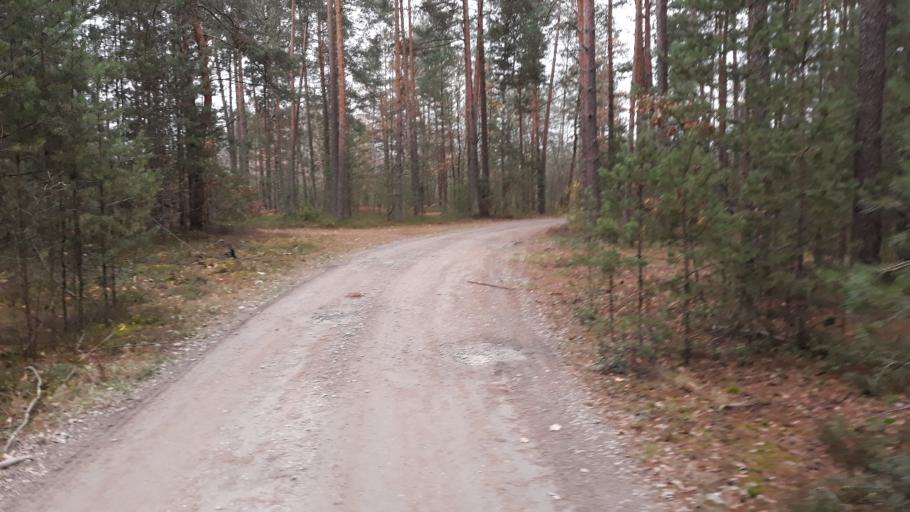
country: PL
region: Lublin Voivodeship
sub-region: Powiat janowski
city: Dzwola
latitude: 50.6515
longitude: 22.5735
